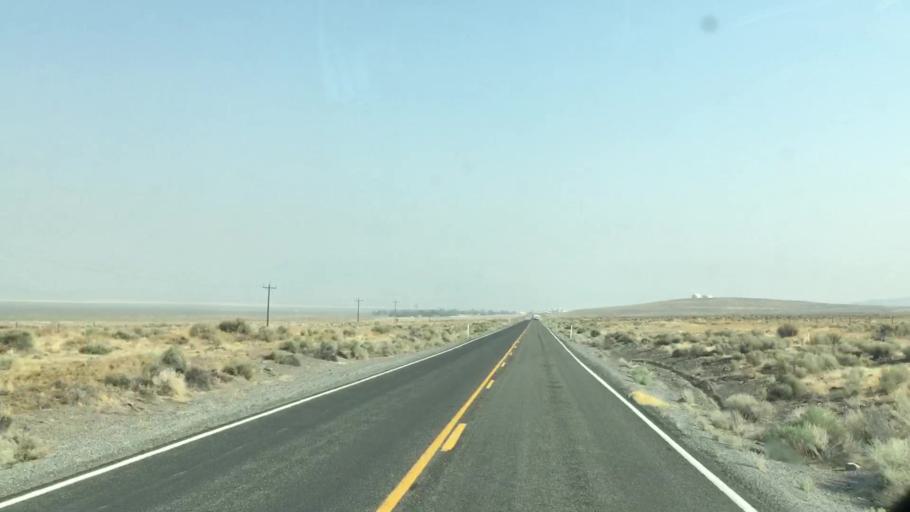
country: US
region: Nevada
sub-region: Pershing County
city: Lovelock
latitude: 40.5515
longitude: -119.3388
